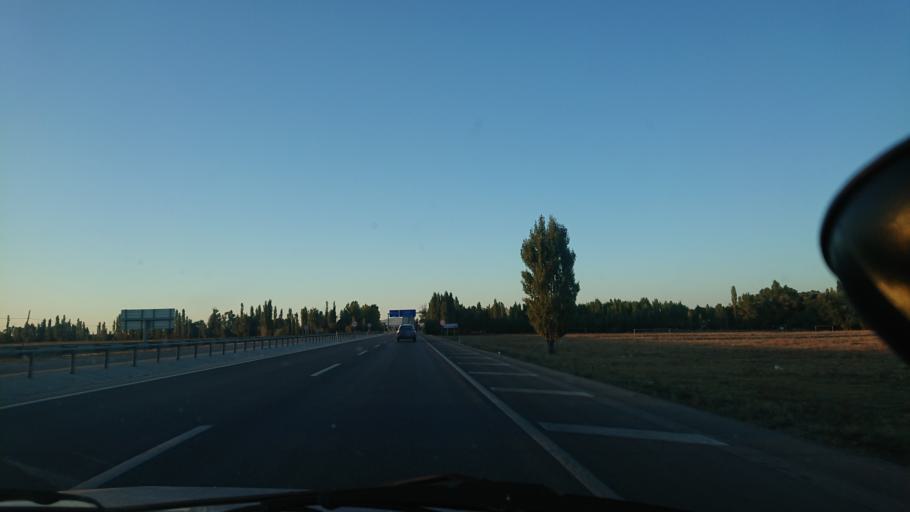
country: TR
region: Eskisehir
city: Mahmudiye
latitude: 39.5662
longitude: 30.9144
